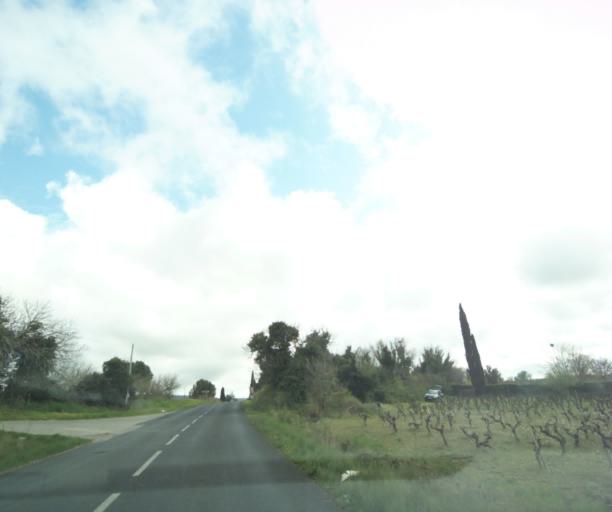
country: FR
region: Languedoc-Roussillon
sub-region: Departement de l'Herault
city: Fabregues
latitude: 43.5610
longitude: 3.7756
